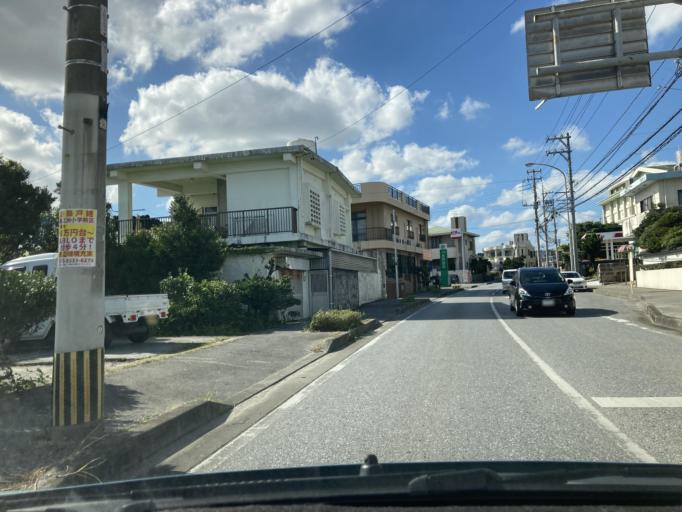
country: JP
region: Okinawa
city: Gushikawa
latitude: 26.3491
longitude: 127.8508
